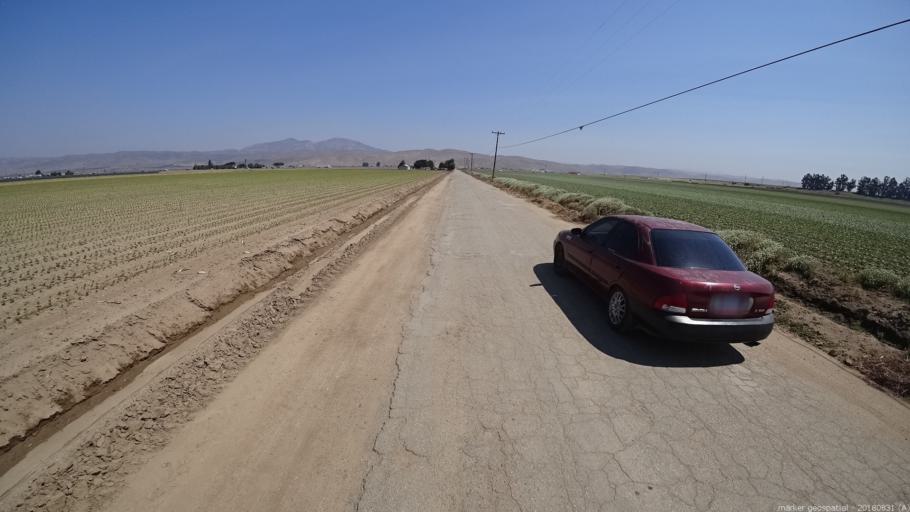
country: US
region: California
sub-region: Monterey County
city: Greenfield
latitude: 36.3500
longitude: -121.2728
